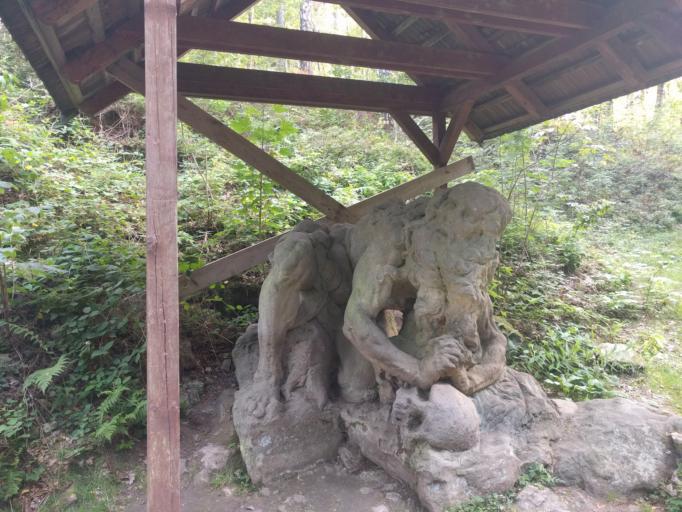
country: CZ
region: Kralovehradecky
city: Dvur Kralove nad Labem
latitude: 50.3981
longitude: 15.8498
